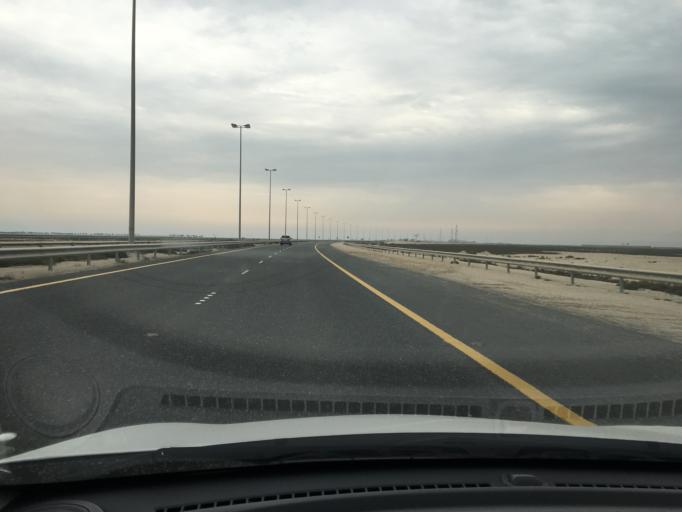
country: BH
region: Central Governorate
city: Dar Kulayb
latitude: 25.8644
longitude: 50.5843
